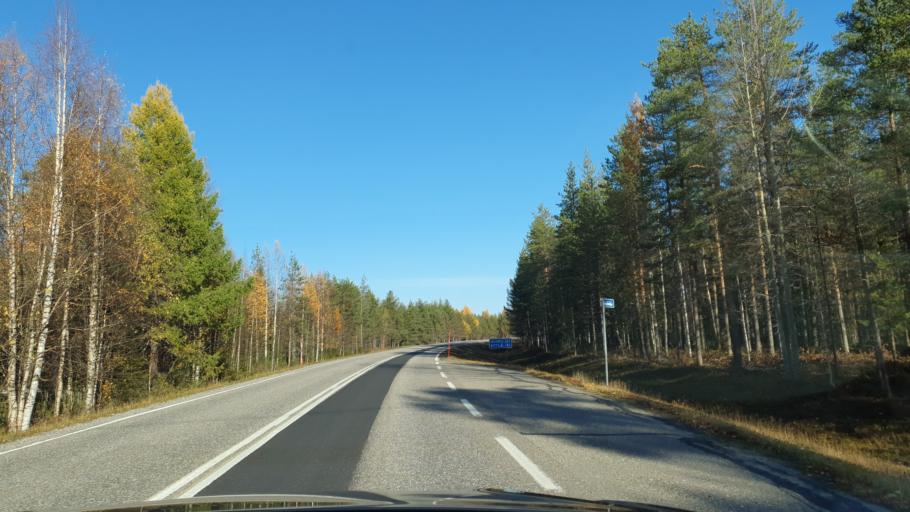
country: FI
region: Lapland
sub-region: Tunturi-Lappi
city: Kittilae
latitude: 67.2939
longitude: 24.8858
